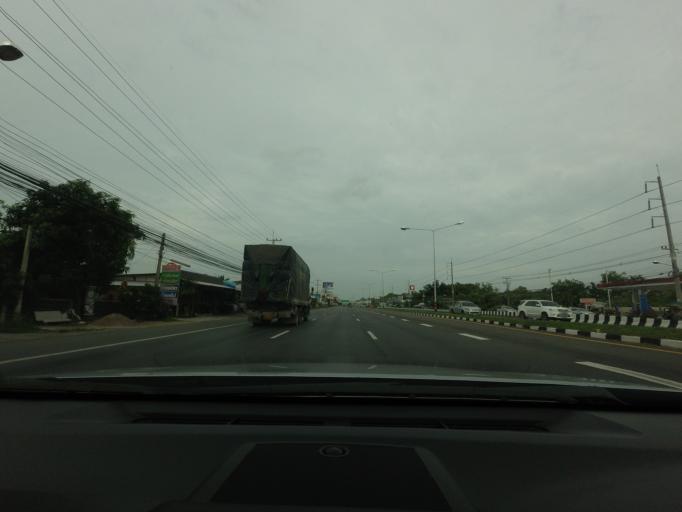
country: TH
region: Phetchaburi
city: Phetchaburi
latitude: 13.1166
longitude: 99.9142
